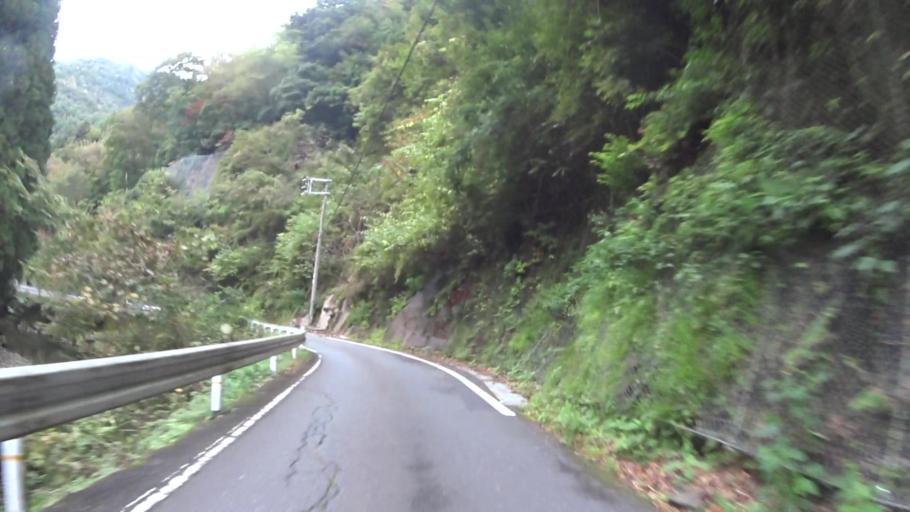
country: JP
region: Fukui
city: Obama
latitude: 35.2975
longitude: 135.6956
